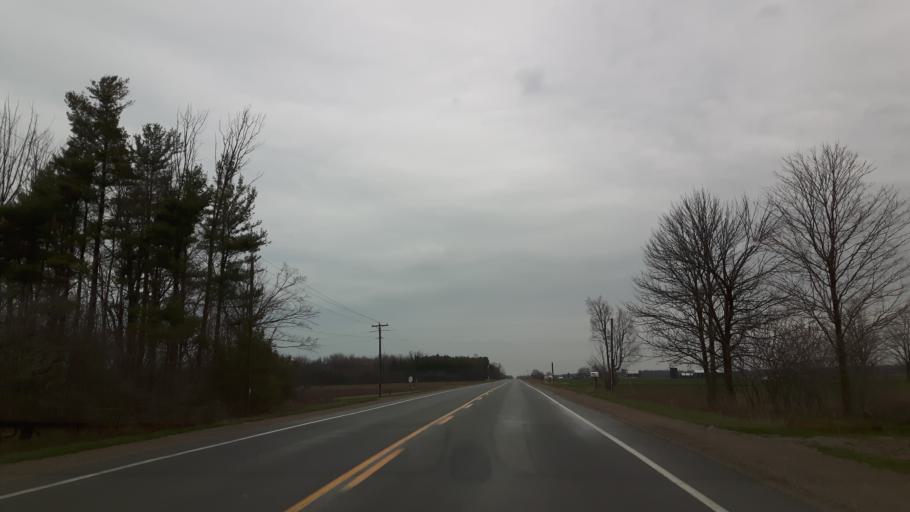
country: CA
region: Ontario
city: Goderich
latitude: 43.6159
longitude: -81.7056
